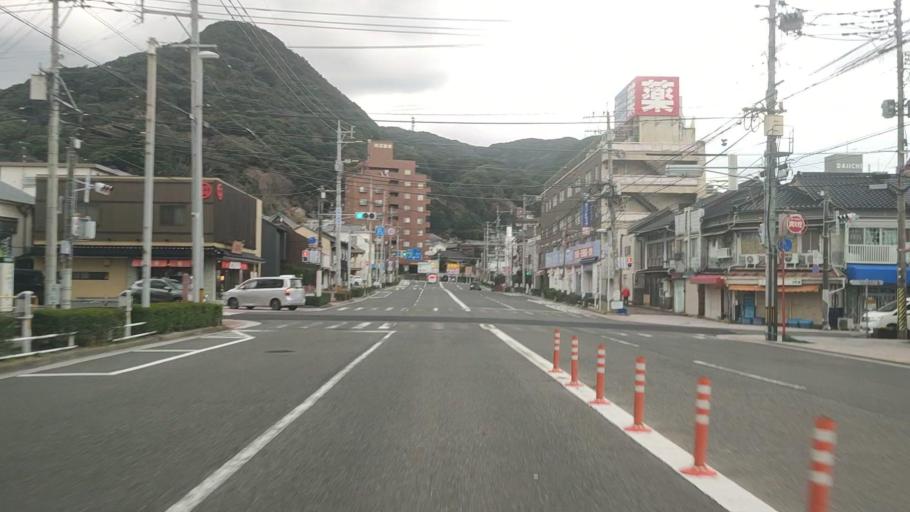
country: JP
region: Yamaguchi
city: Shimonoseki
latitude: 33.9451
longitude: 130.9670
